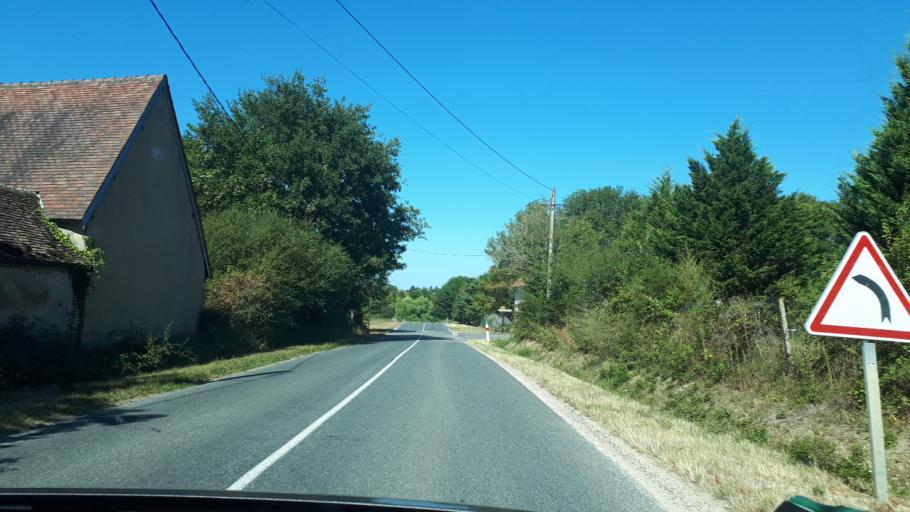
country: FR
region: Centre
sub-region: Departement du Loiret
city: Coullons
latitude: 47.6232
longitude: 2.5026
